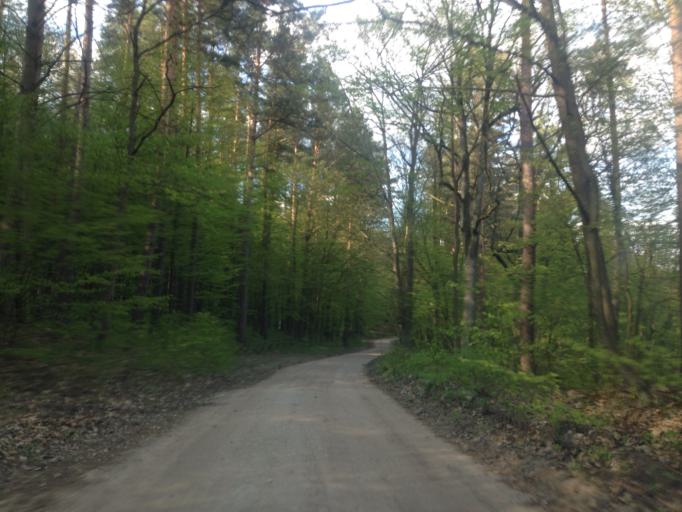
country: PL
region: Kujawsko-Pomorskie
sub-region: Powiat brodnicki
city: Gorzno
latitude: 53.2111
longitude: 19.7262
